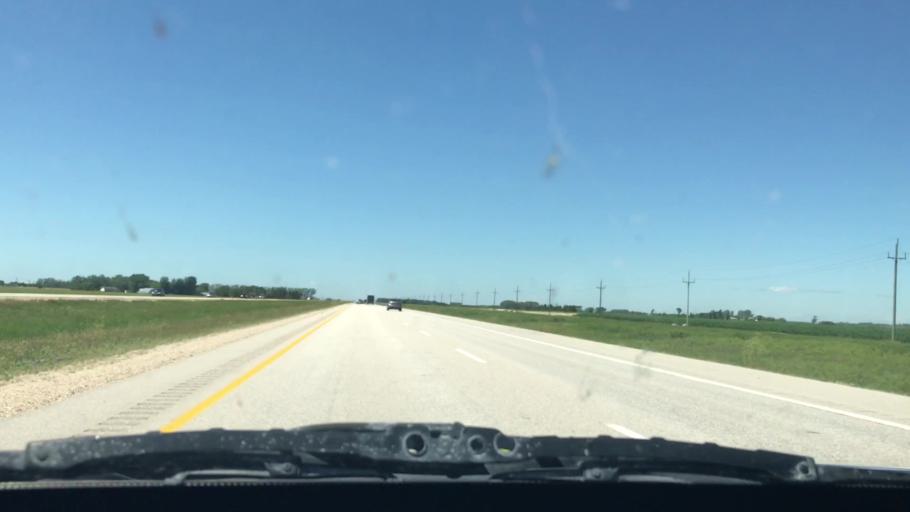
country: CA
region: Manitoba
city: Steinbach
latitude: 49.7275
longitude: -96.7117
